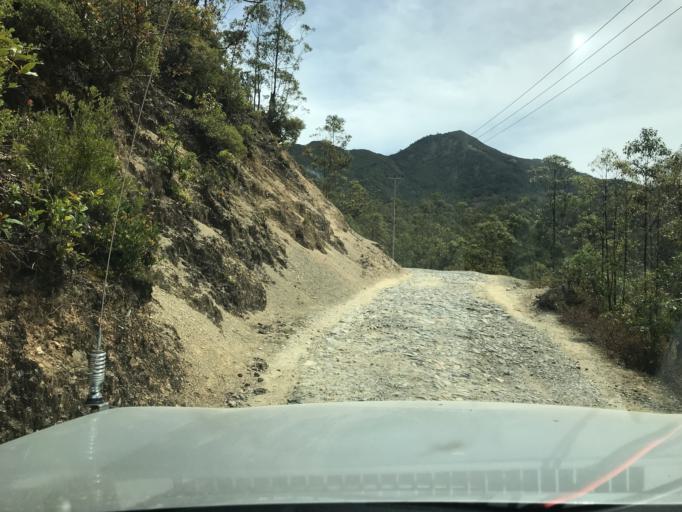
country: TL
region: Ainaro
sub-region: Ainaro
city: Ainaro
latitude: -8.8846
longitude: 125.5256
